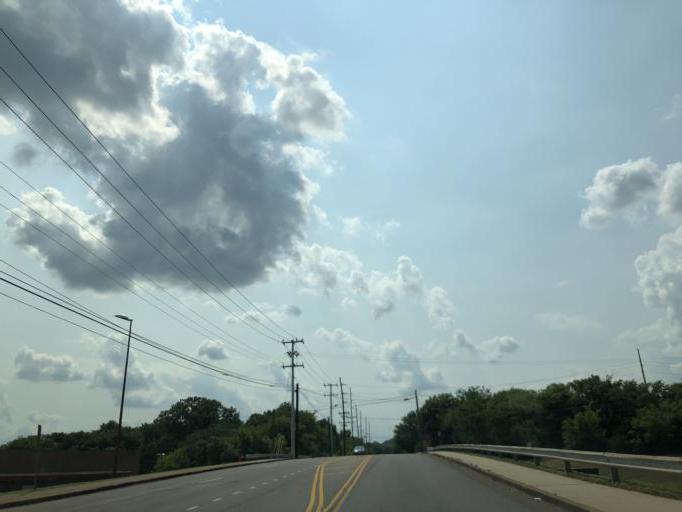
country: US
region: Tennessee
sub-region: Davidson County
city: Goodlettsville
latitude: 36.2482
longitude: -86.7218
